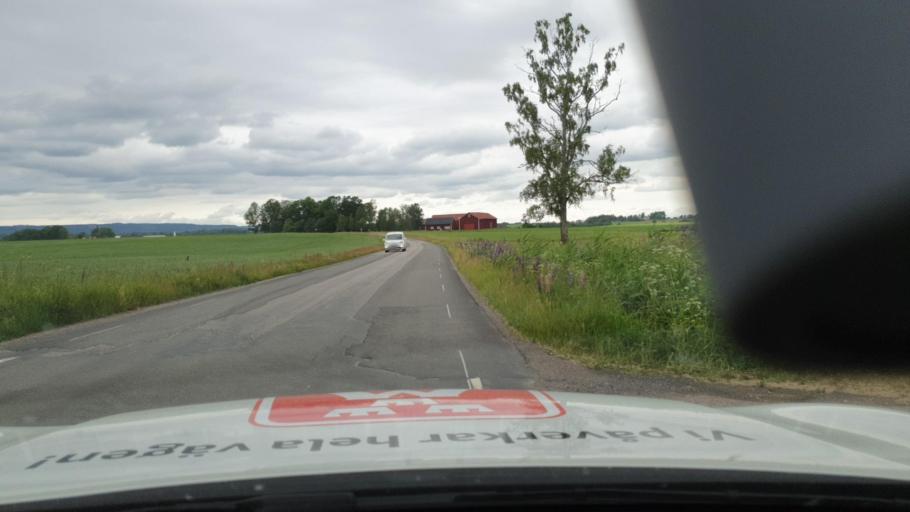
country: SE
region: Vaestra Goetaland
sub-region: Skovde Kommun
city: Skoevde
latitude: 58.3807
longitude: 13.9220
